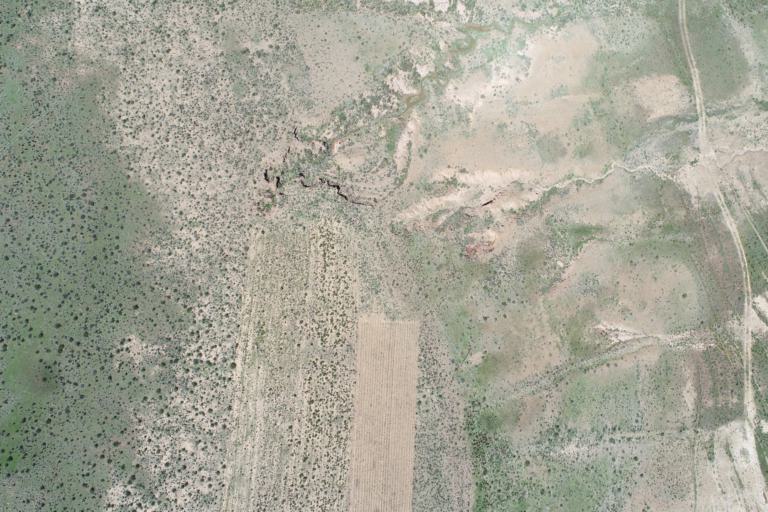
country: BO
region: La Paz
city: Curahuara de Carangas
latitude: -17.3198
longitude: -68.5042
